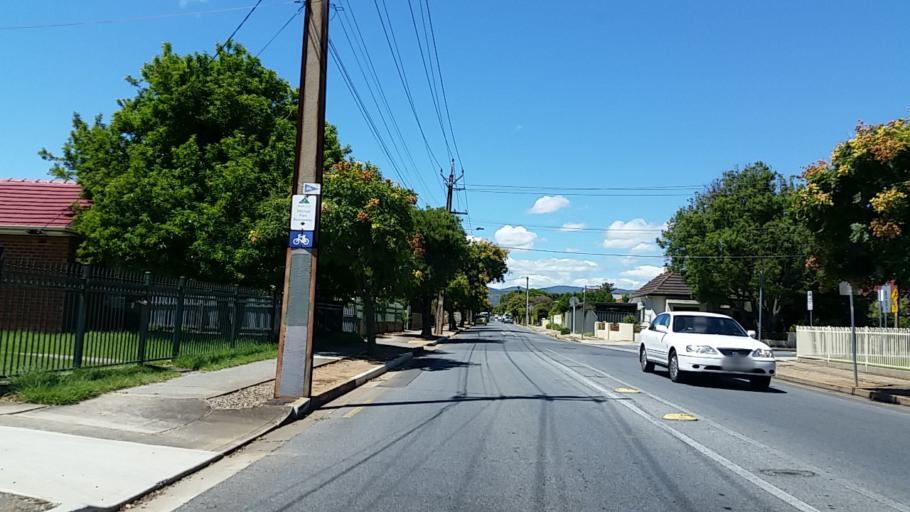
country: AU
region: South Australia
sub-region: Marion
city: South Plympton
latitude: -34.9705
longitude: 138.5639
